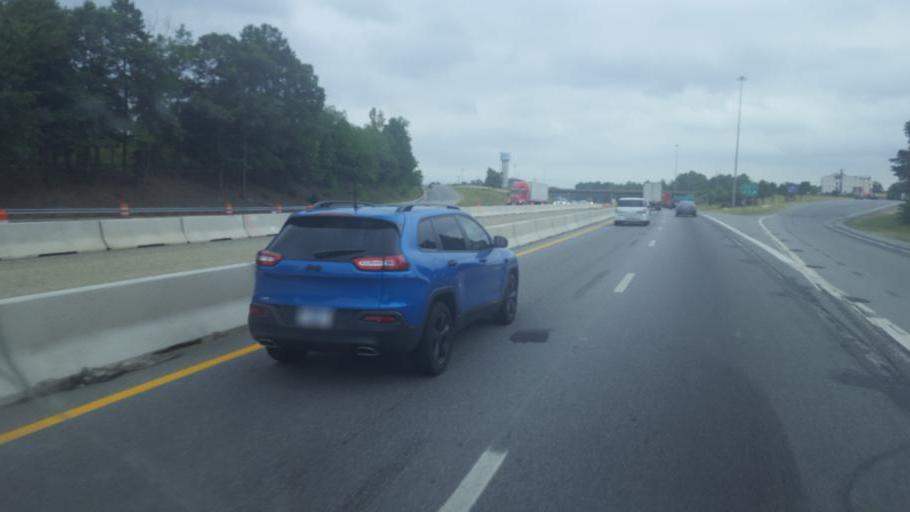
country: US
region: North Carolina
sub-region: Gaston County
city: Davidson
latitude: 35.5505
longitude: -80.8579
